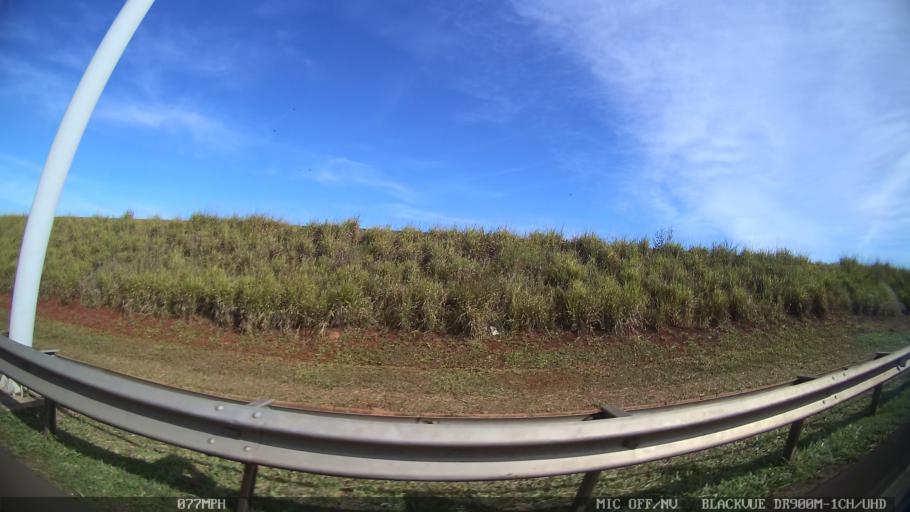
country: BR
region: Sao Paulo
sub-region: Cordeiropolis
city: Cordeiropolis
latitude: -22.4801
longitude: -47.3991
